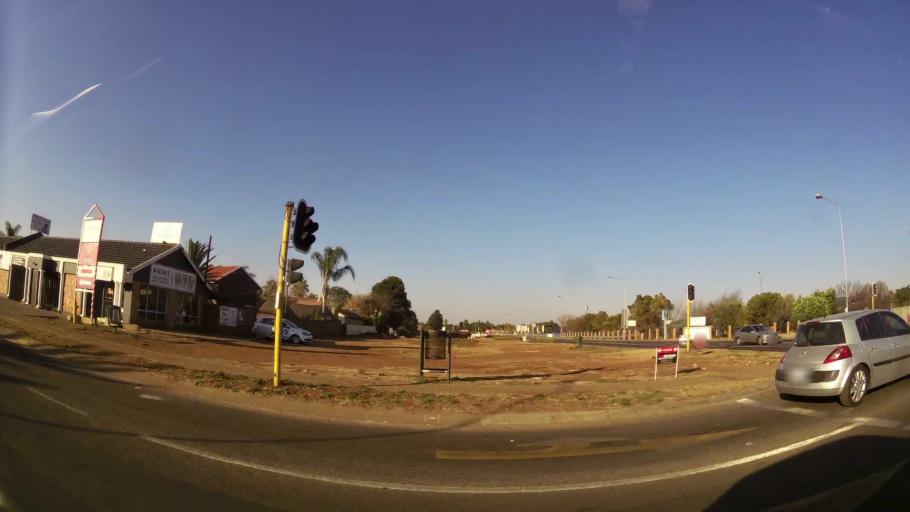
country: ZA
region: Gauteng
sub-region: City of Tshwane Metropolitan Municipality
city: Centurion
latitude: -25.8679
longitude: 28.1518
